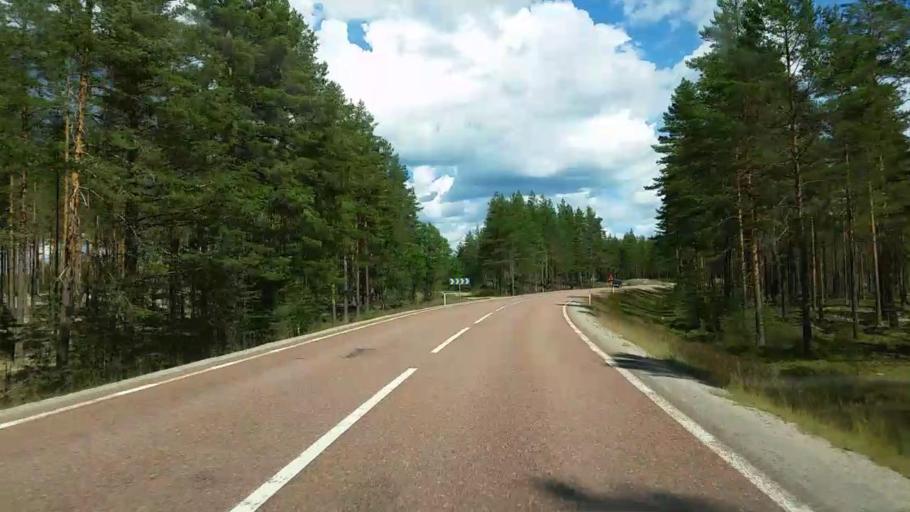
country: SE
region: Gaevleborg
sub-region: Ovanakers Kommun
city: Edsbyn
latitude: 61.3510
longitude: 15.5780
